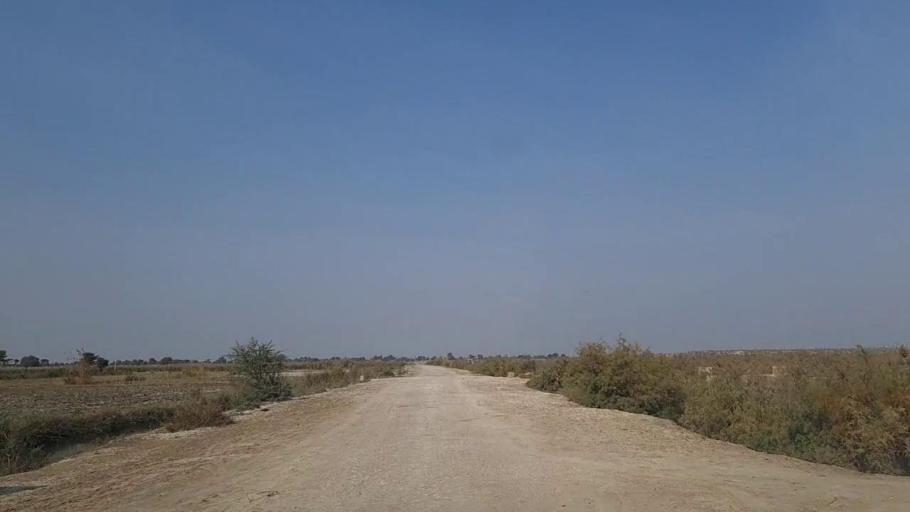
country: PK
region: Sindh
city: Daur
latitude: 26.5042
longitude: 68.4796
